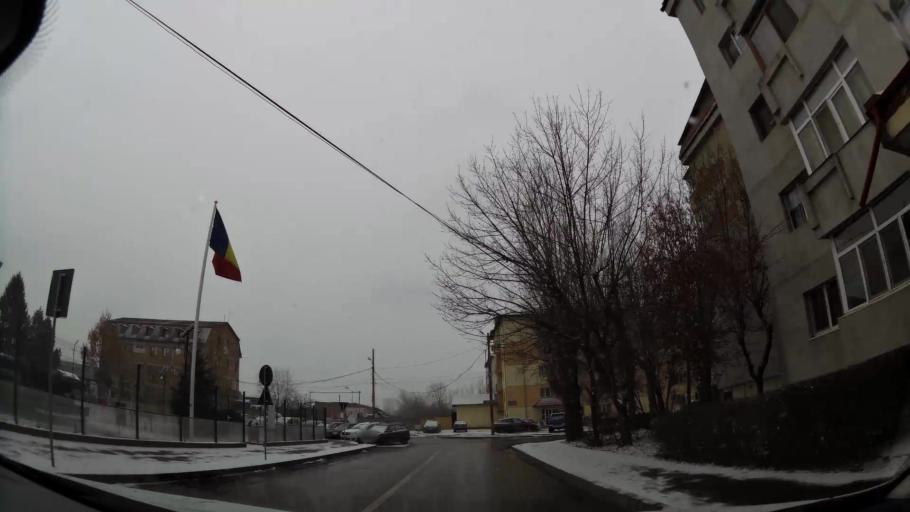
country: RO
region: Dambovita
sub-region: Municipiul Targoviste
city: Targoviste
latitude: 44.9154
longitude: 25.4704
